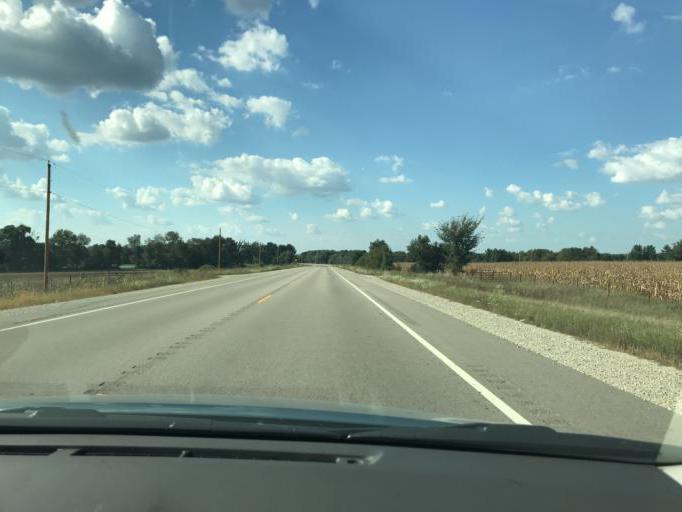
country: US
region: Wisconsin
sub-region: Green County
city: Brodhead
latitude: 42.5804
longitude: -89.3788
